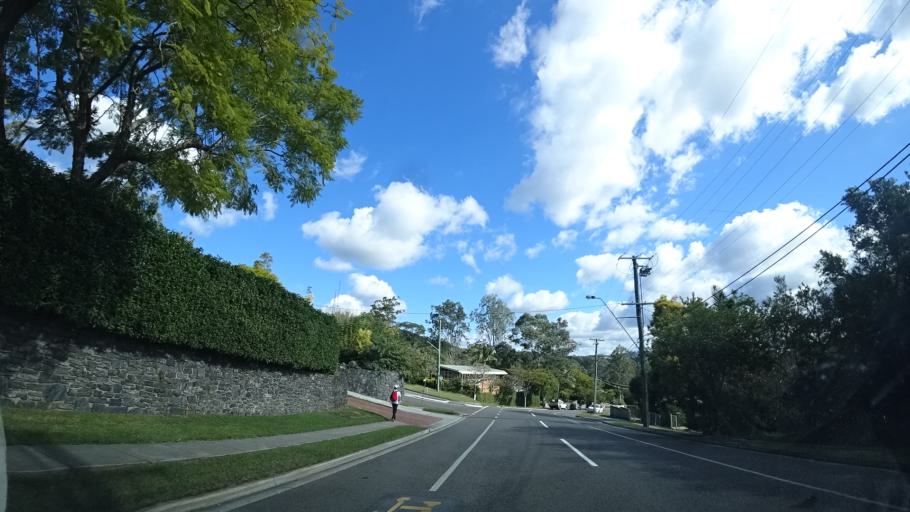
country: AU
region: Queensland
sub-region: Brisbane
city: Taringa
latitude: -27.4487
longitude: 152.9574
